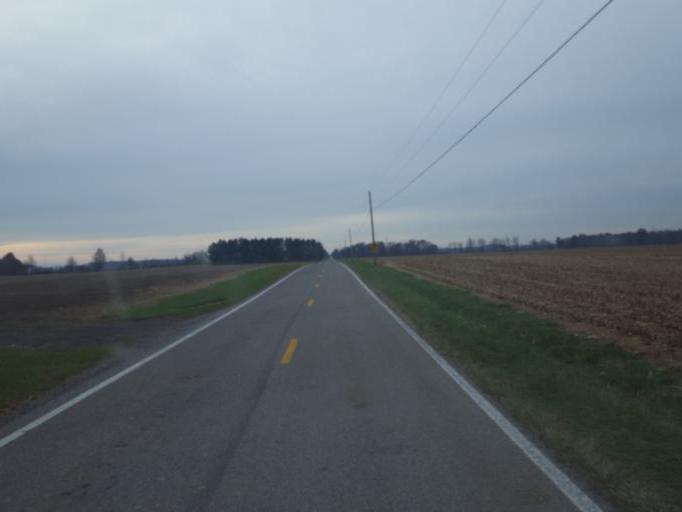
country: US
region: Ohio
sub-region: Delaware County
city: Ashley
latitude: 40.3920
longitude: -83.0142
